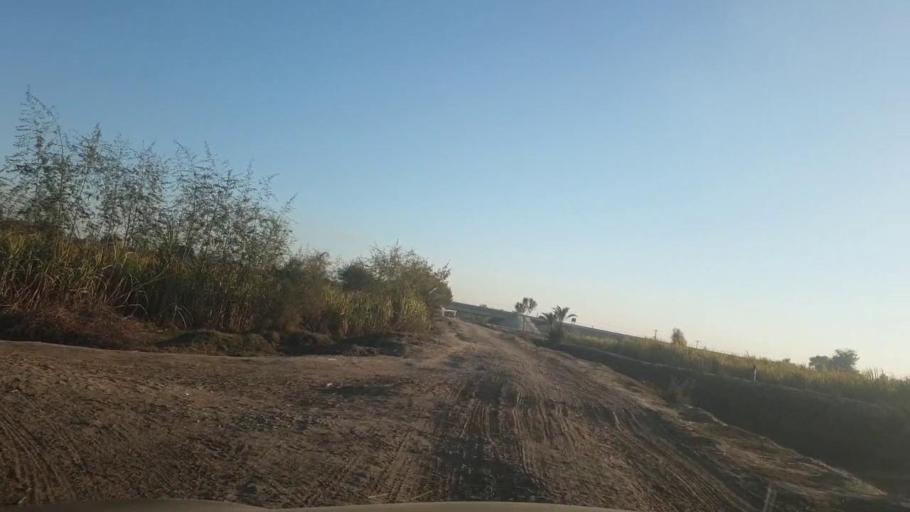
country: PK
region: Sindh
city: Ghotki
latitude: 28.0106
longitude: 69.2689
